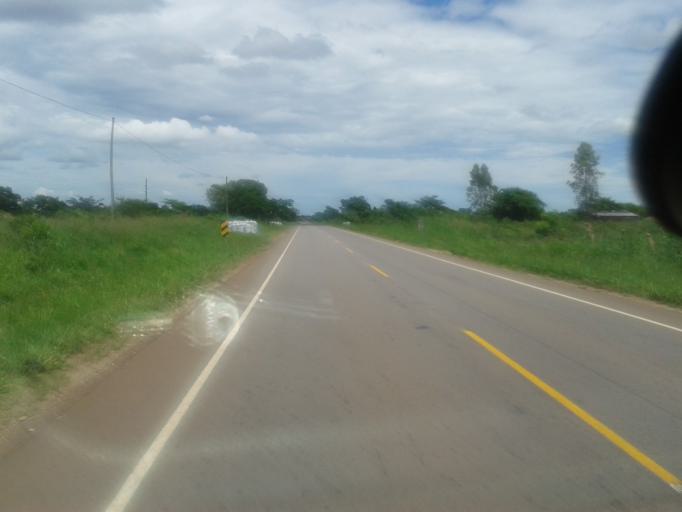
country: UG
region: Western Region
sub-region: Kiryandongo District
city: Masindi Port
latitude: 1.7247
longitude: 32.0262
